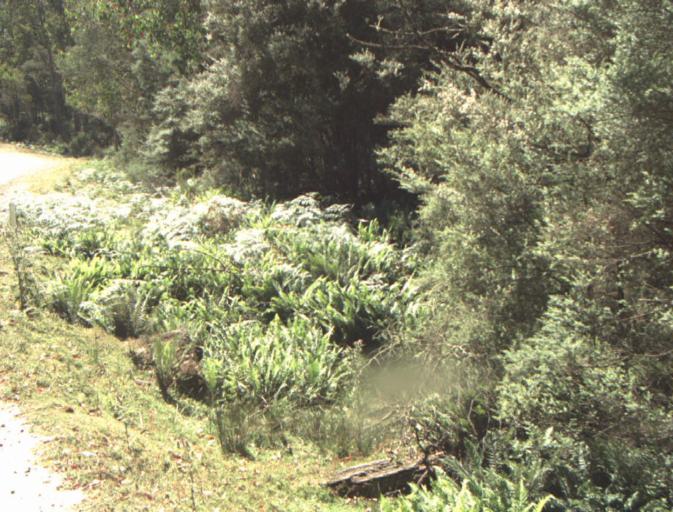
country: AU
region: Tasmania
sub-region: Dorset
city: Scottsdale
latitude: -41.3858
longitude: 147.5027
